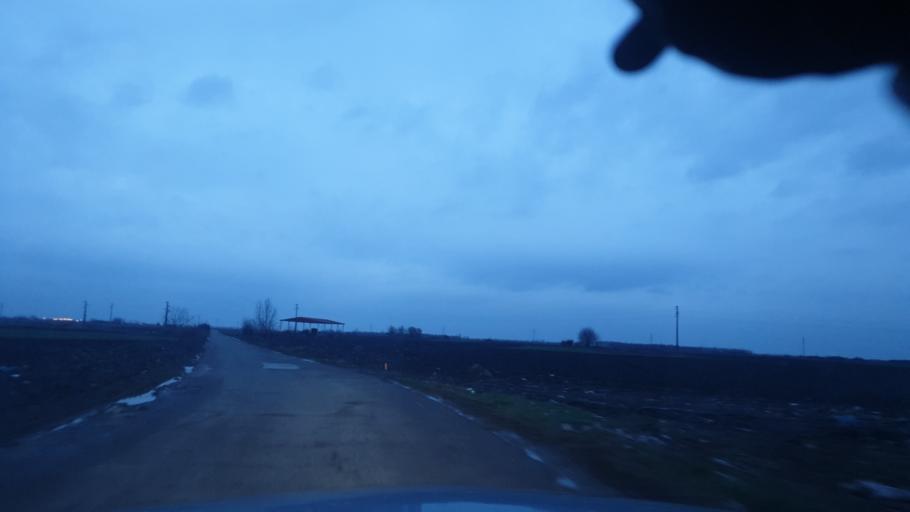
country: RS
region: Autonomna Pokrajina Vojvodina
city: Nova Pazova
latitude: 44.9338
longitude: 20.2140
